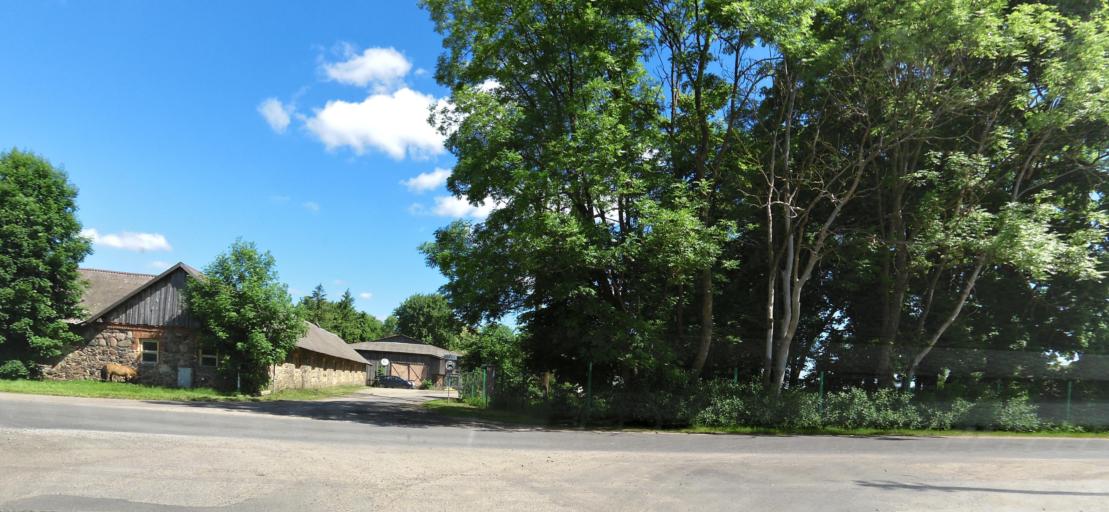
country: LT
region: Vilnius County
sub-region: Vilnius
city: Fabijoniskes
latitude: 54.8252
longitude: 25.2809
